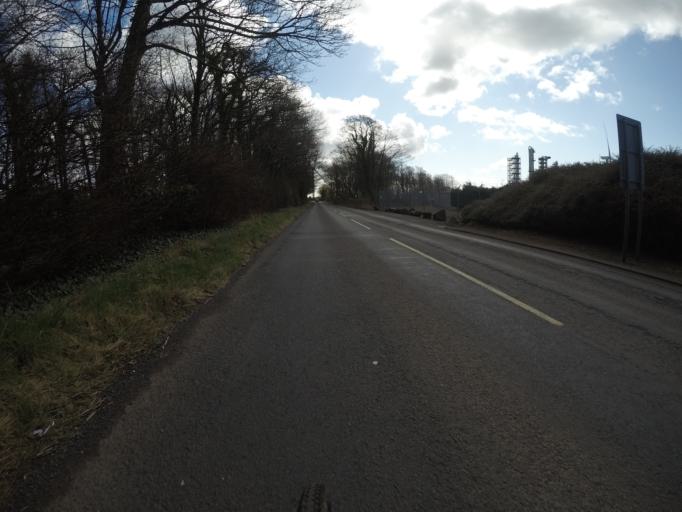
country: GB
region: Scotland
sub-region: North Ayrshire
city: Dreghorn
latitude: 55.5959
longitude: -4.6249
